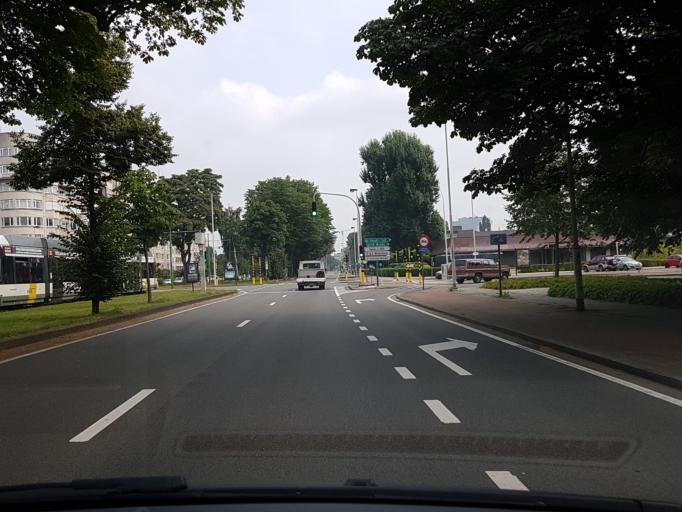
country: BE
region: Flanders
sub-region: Provincie Antwerpen
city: Antwerpen
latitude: 51.1894
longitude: 4.3960
